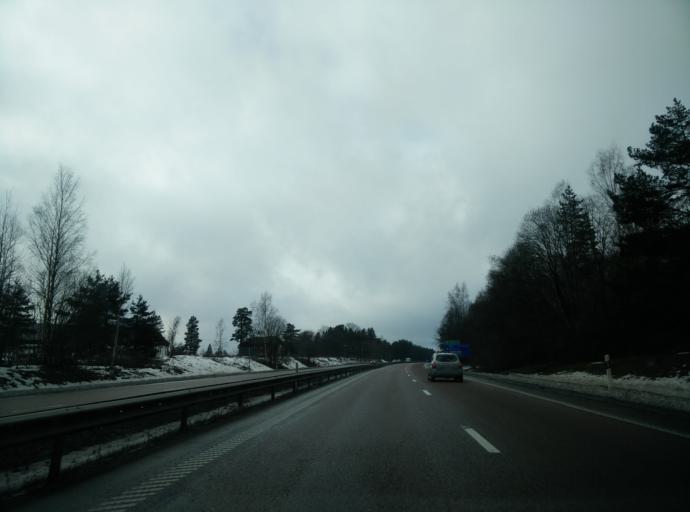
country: SE
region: Gaevleborg
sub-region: Gavle Kommun
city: Valbo
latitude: 60.6346
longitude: 17.0048
